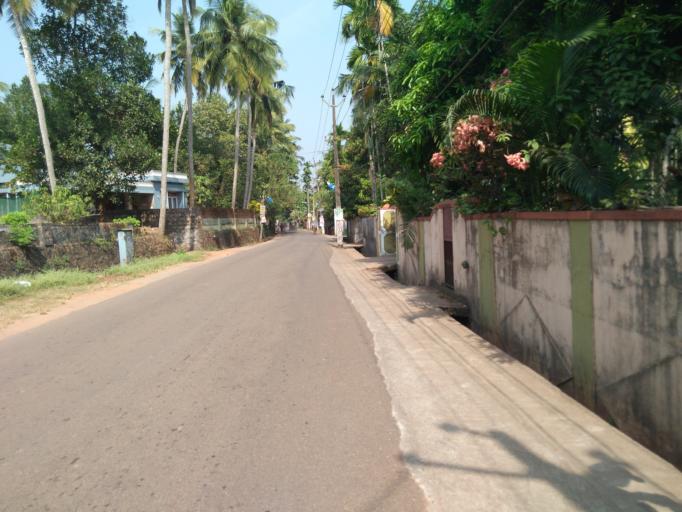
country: IN
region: Kerala
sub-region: Kozhikode
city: Kunnamangalam
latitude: 11.2935
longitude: 75.8370
